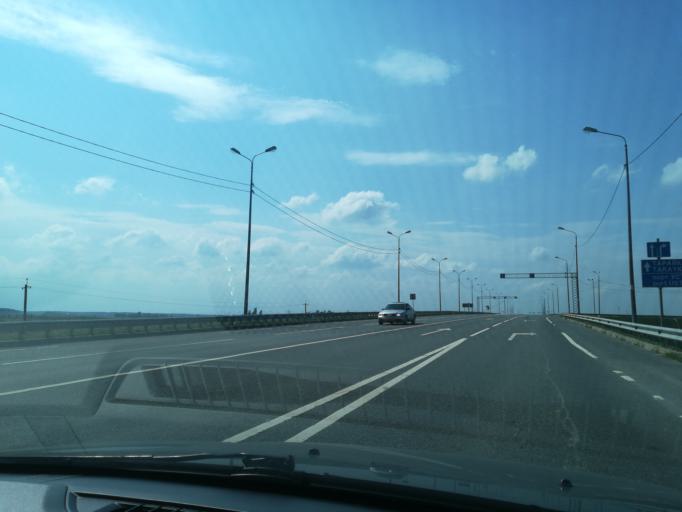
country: RU
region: Leningrad
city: Kingisepp
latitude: 59.5721
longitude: 28.7713
